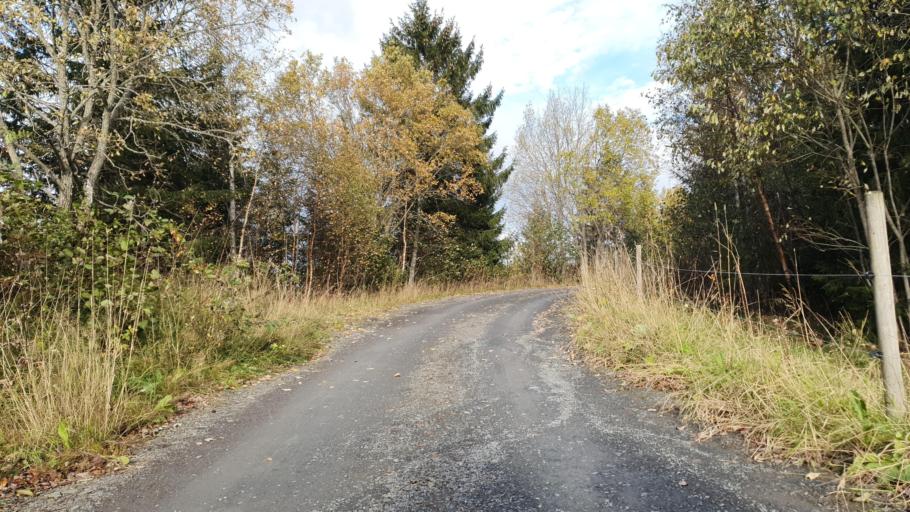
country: NO
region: Sor-Trondelag
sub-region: Klaebu
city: Klaebu
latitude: 63.2898
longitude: 10.4609
